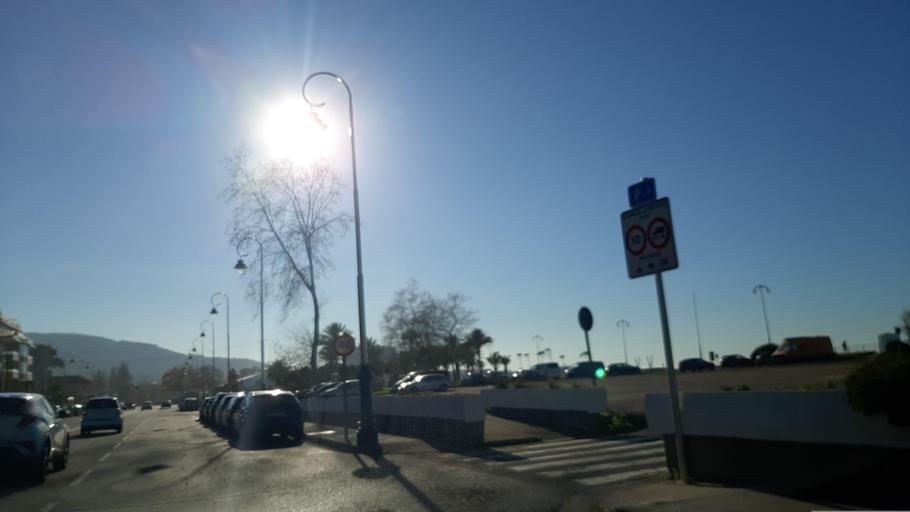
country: ES
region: Galicia
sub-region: Provincia de Pontevedra
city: Cangas
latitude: 42.2083
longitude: -8.7756
